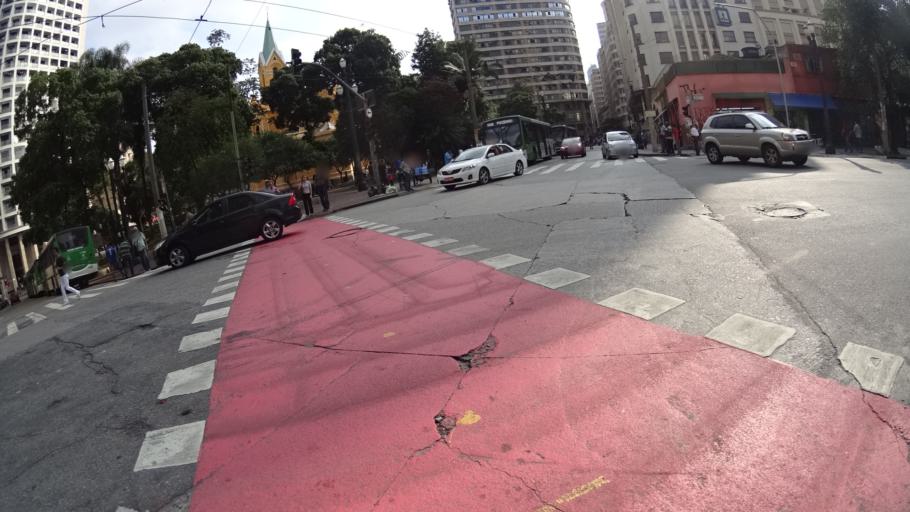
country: BR
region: Sao Paulo
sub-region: Sao Paulo
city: Sao Paulo
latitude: -23.5422
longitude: -46.6375
